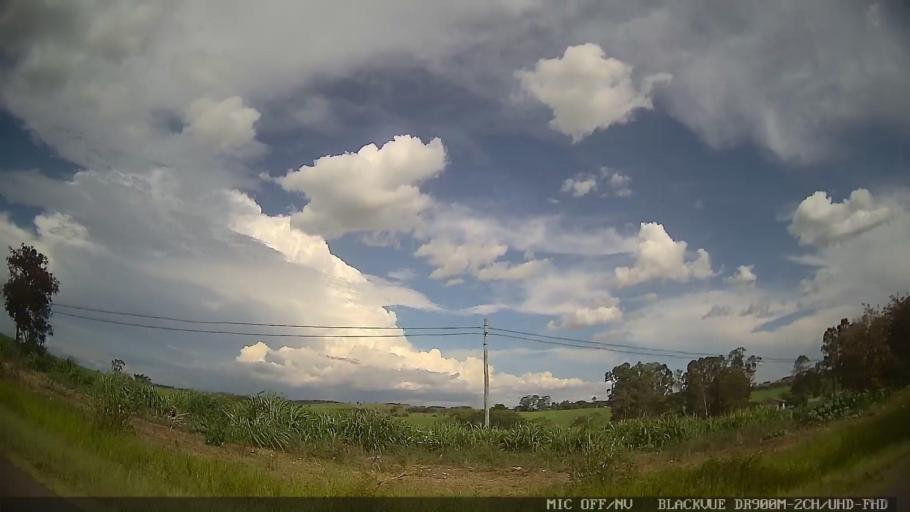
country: BR
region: Sao Paulo
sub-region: Conchas
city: Conchas
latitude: -23.0524
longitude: -47.9591
